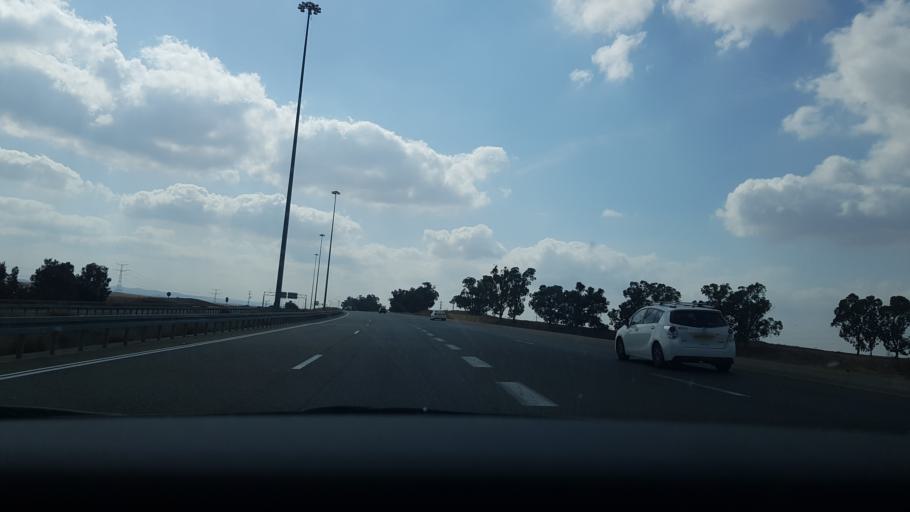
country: IL
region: Southern District
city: Qiryat Gat
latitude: 31.5100
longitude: 34.7817
